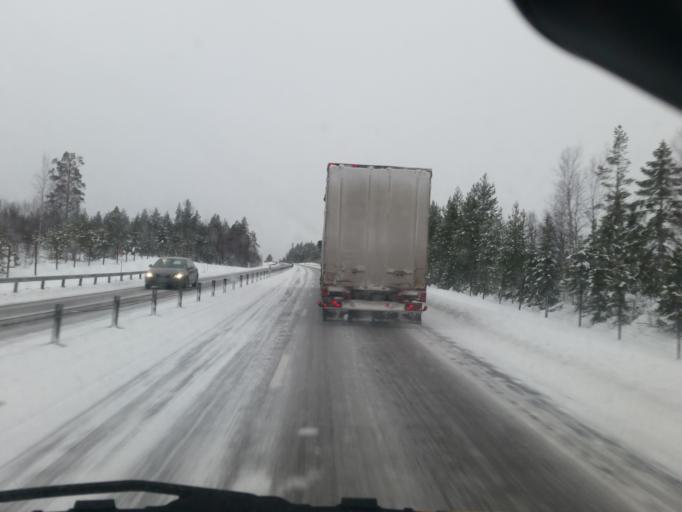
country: SE
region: Norrbotten
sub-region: Pitea Kommun
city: Pitea
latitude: 65.2008
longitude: 21.5142
